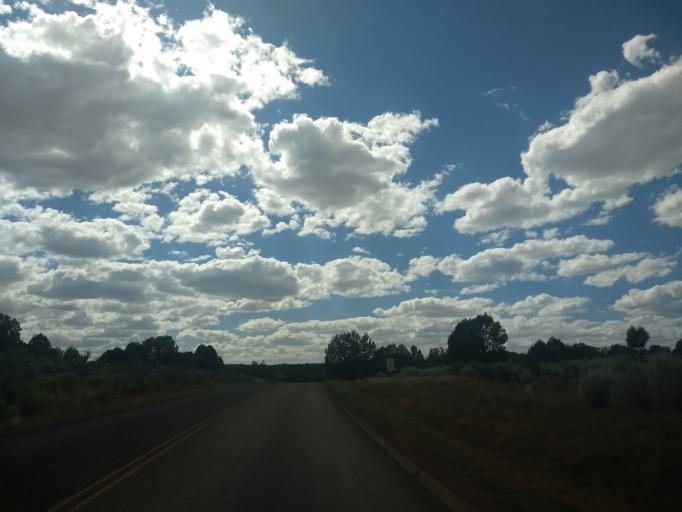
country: US
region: Utah
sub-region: Kane County
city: Kanab
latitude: 37.1453
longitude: -112.5618
